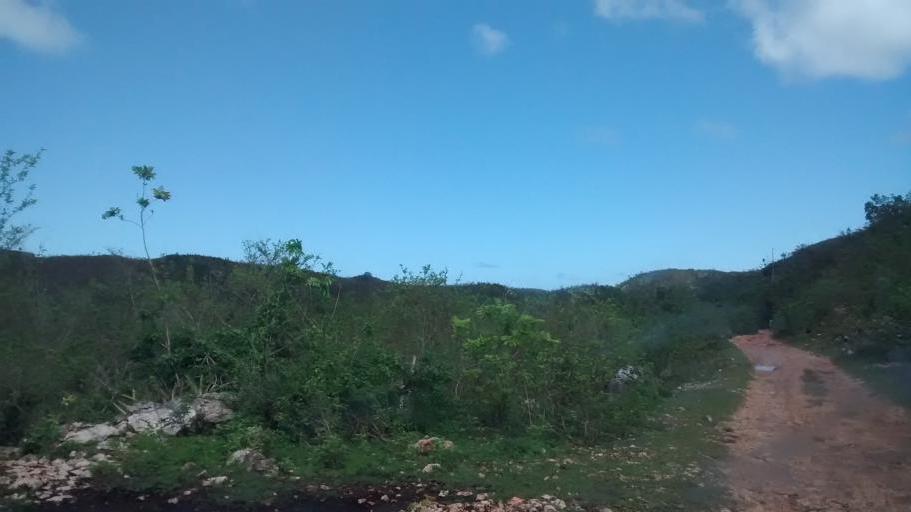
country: HT
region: Grandans
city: Corail
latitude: 18.5412
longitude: -73.9183
